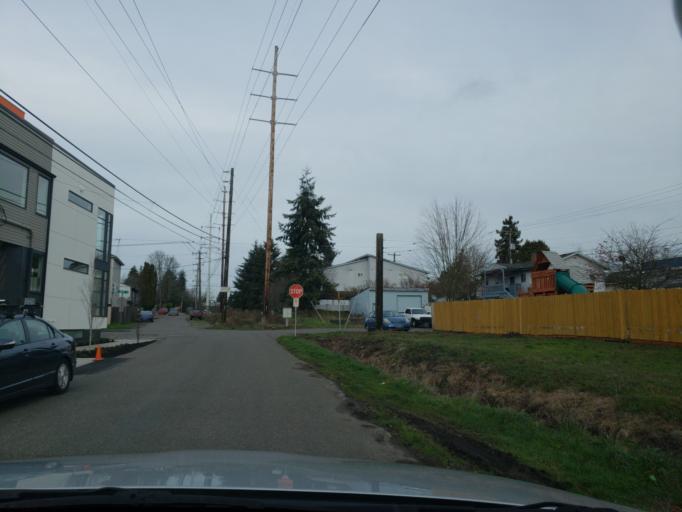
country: US
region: Washington
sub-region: King County
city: Shoreline
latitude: 47.7033
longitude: -122.3508
